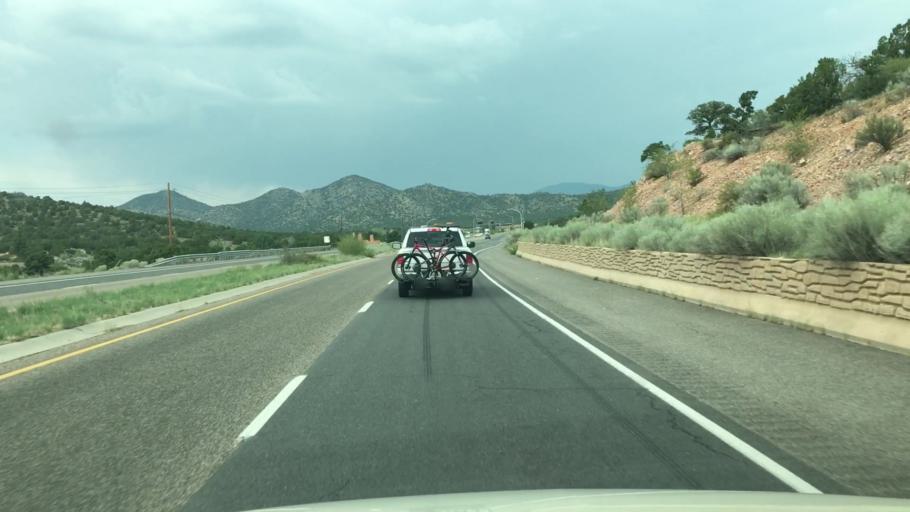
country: US
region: New Mexico
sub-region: Santa Fe County
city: Eldorado at Santa Fe
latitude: 35.5462
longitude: -105.8833
